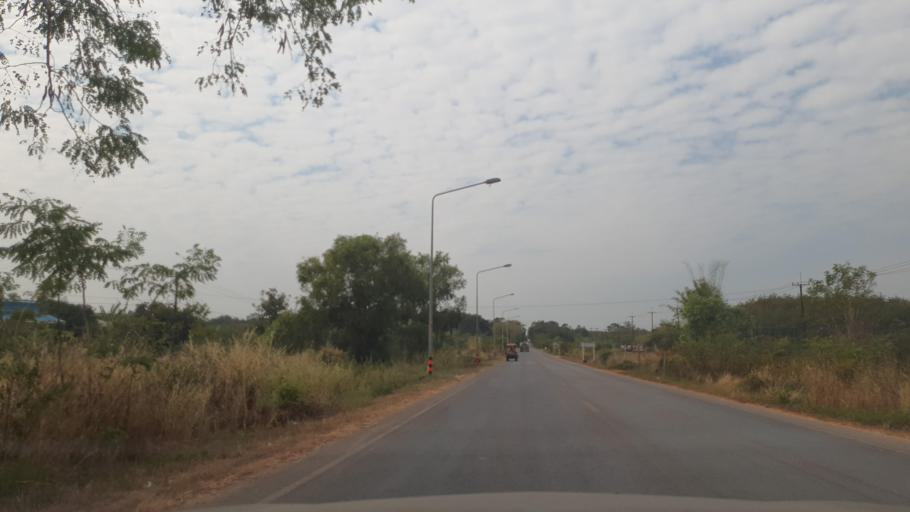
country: TH
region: Changwat Bueng Kan
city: Bung Khla
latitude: 18.3049
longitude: 103.9651
